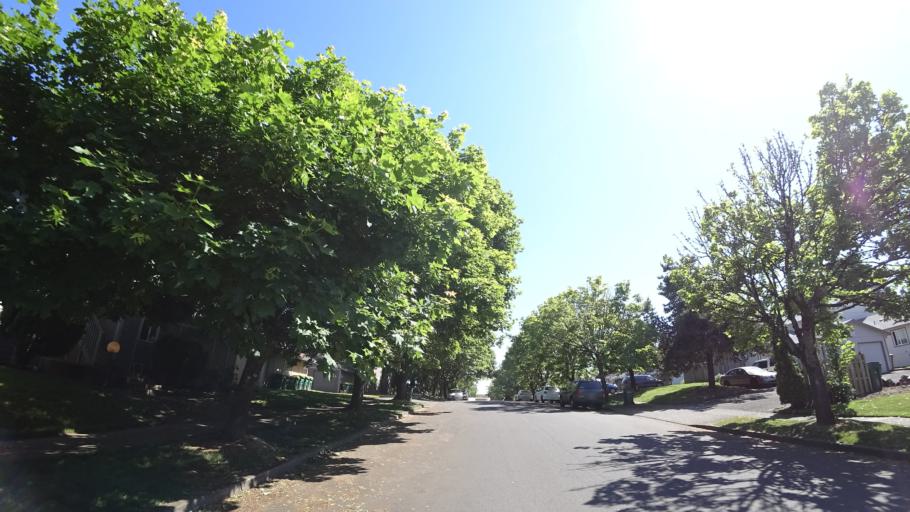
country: US
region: Oregon
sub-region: Washington County
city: Tigard
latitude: 45.4490
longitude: -122.8027
